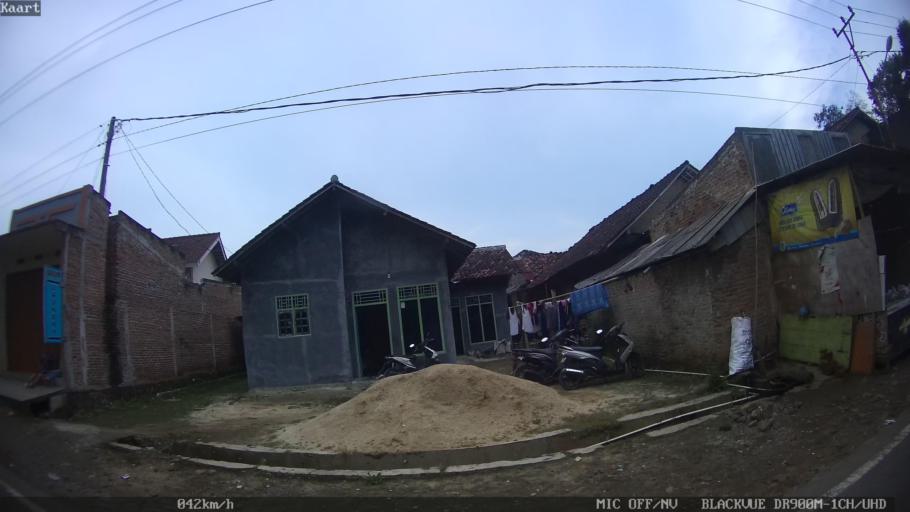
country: ID
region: Lampung
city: Bandarlampung
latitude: -5.4305
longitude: 105.2104
